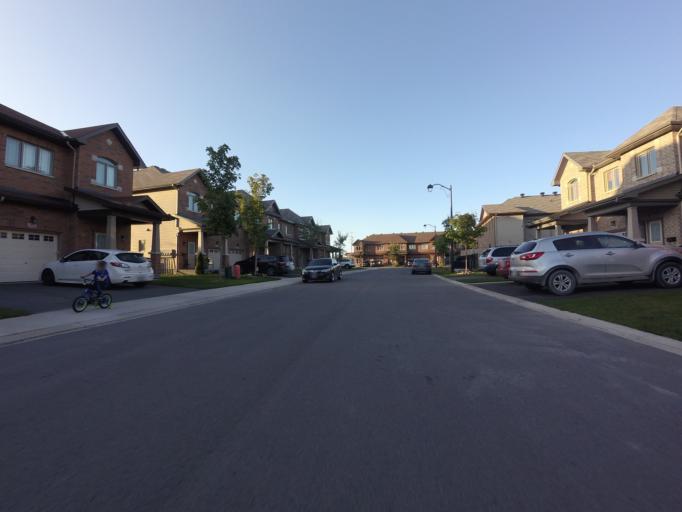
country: CA
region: Ontario
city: Bells Corners
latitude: 45.2816
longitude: -75.7487
